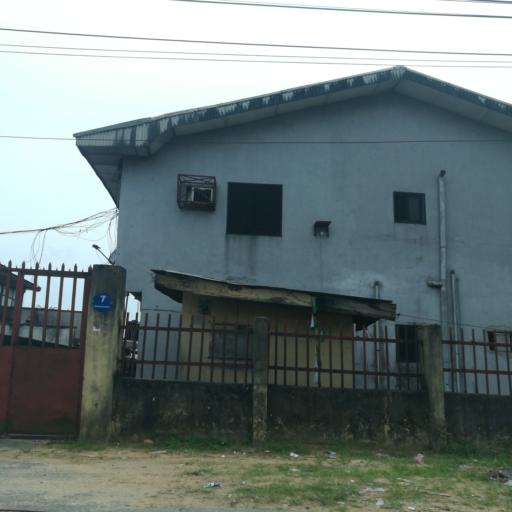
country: NG
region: Rivers
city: Port Harcourt
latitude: 4.8038
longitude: 7.0059
